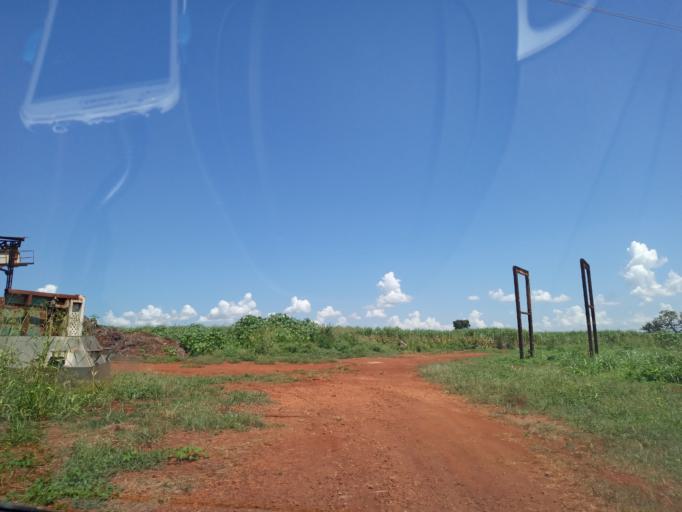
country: BR
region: Goias
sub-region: Itumbiara
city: Itumbiara
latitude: -18.4381
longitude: -49.1679
